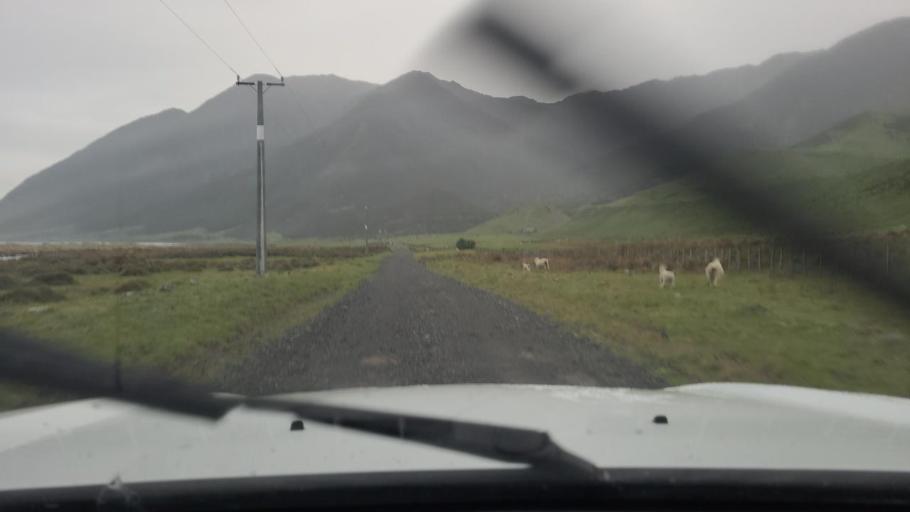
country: NZ
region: Wellington
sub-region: South Wairarapa District
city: Waipawa
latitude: -41.5677
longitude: 175.3800
